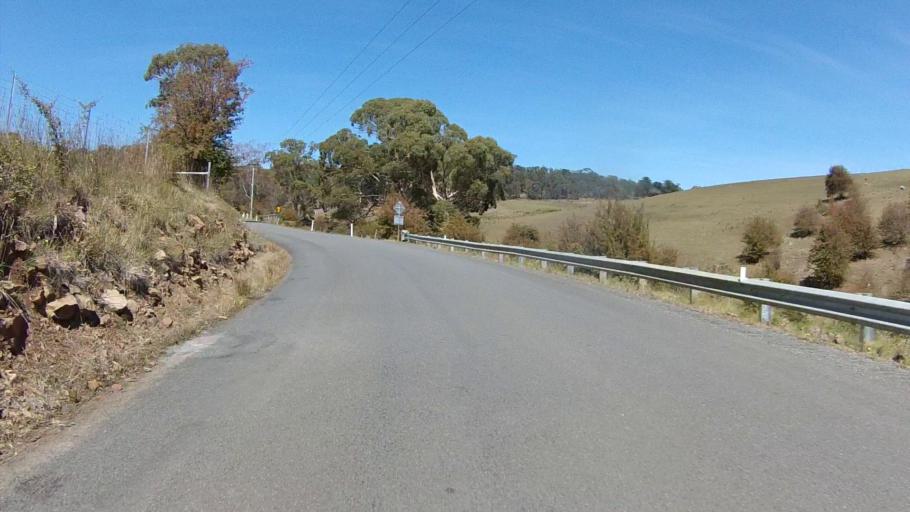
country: AU
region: Tasmania
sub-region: Sorell
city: Sorell
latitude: -42.7628
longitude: 147.6494
